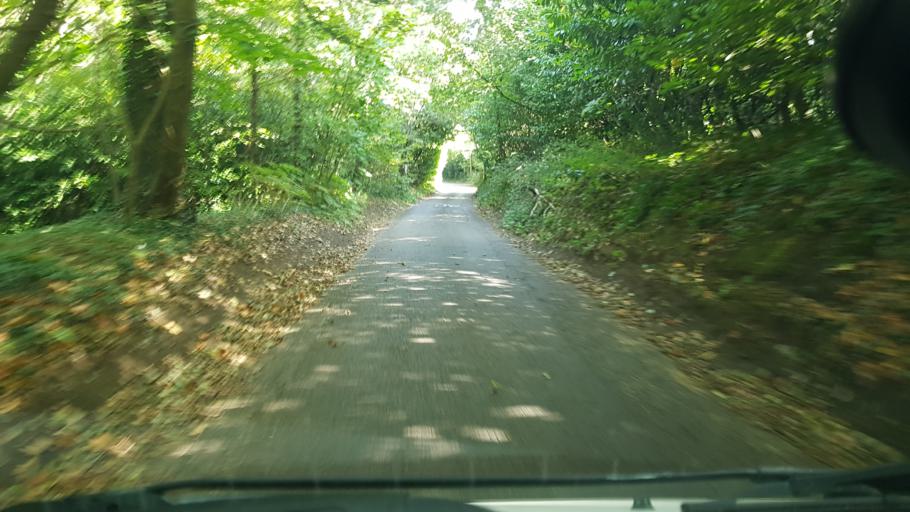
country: GB
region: England
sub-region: Surrey
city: Guildford
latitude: 51.2230
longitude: -0.5892
